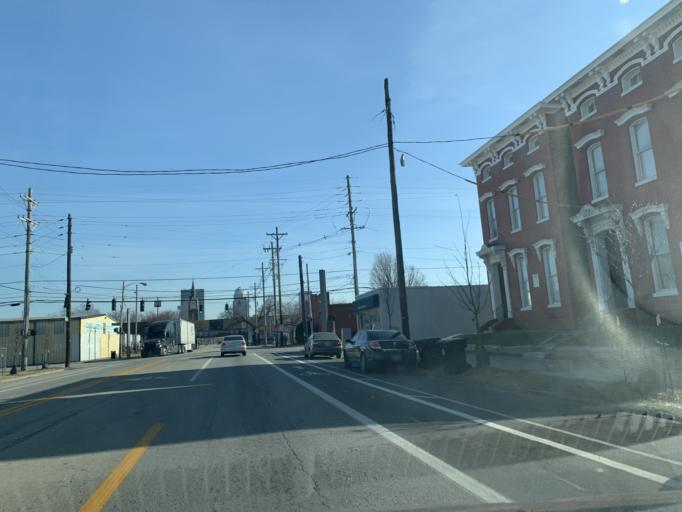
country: US
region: Kentucky
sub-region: Jefferson County
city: Louisville
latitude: 38.2573
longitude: -85.7757
